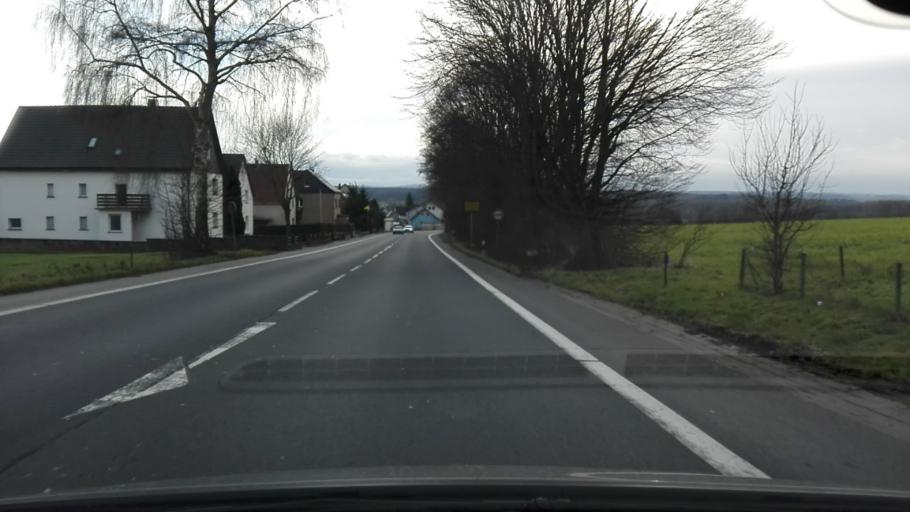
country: DE
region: North Rhine-Westphalia
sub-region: Regierungsbezirk Arnsberg
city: Unna
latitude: 51.4807
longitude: 7.7084
